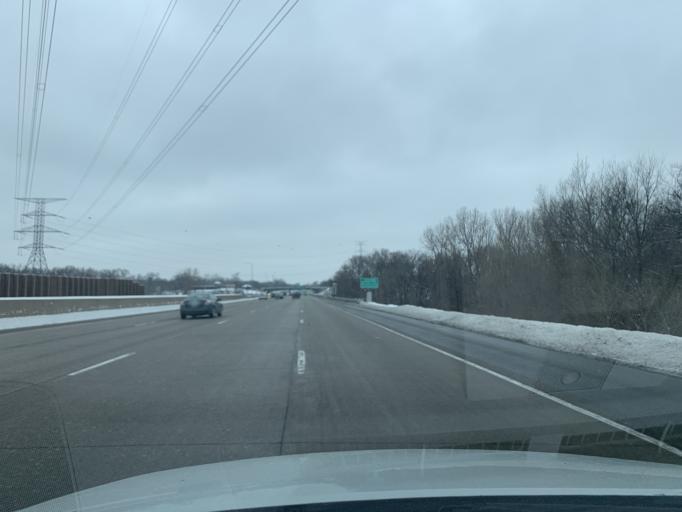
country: US
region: Minnesota
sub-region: Anoka County
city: Coon Rapids
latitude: 45.1326
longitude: -93.2966
